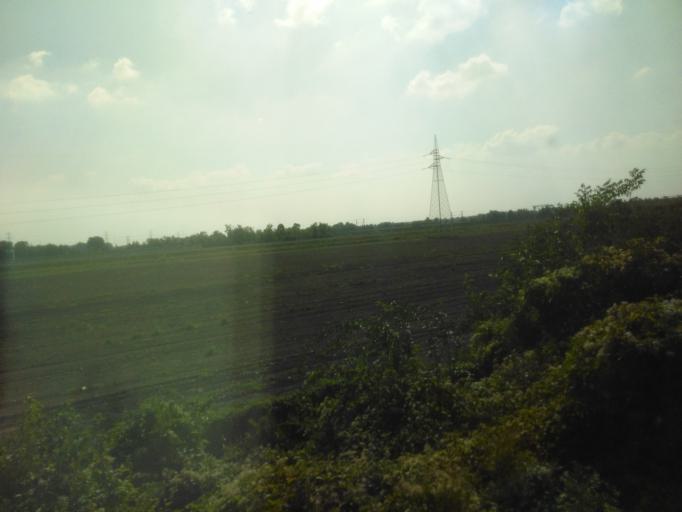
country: IT
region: Lombardy
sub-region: Provincia di Bergamo
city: Casirate d'Adda
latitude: 45.5128
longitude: 9.5464
